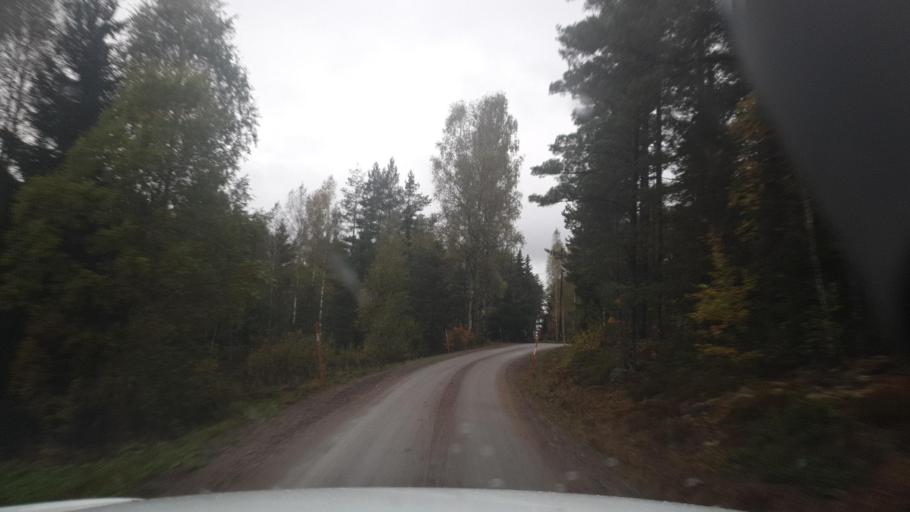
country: SE
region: Vaermland
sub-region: Sunne Kommun
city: Sunne
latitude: 59.6393
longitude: 13.0600
